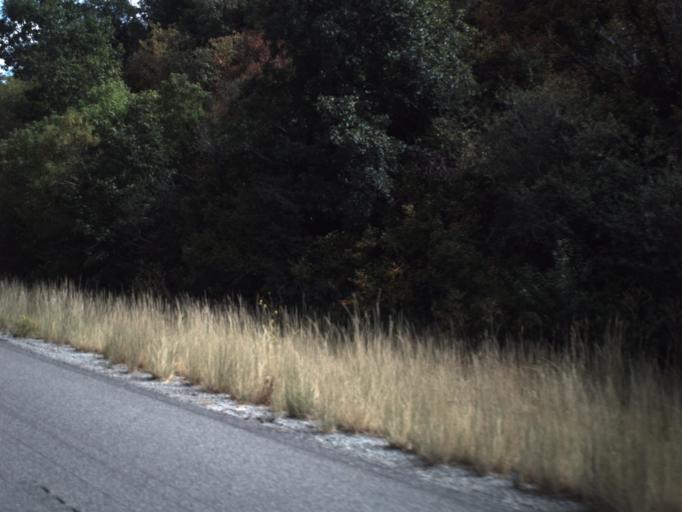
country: US
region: Utah
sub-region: Cache County
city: Wellsville
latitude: 41.6040
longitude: -111.9619
